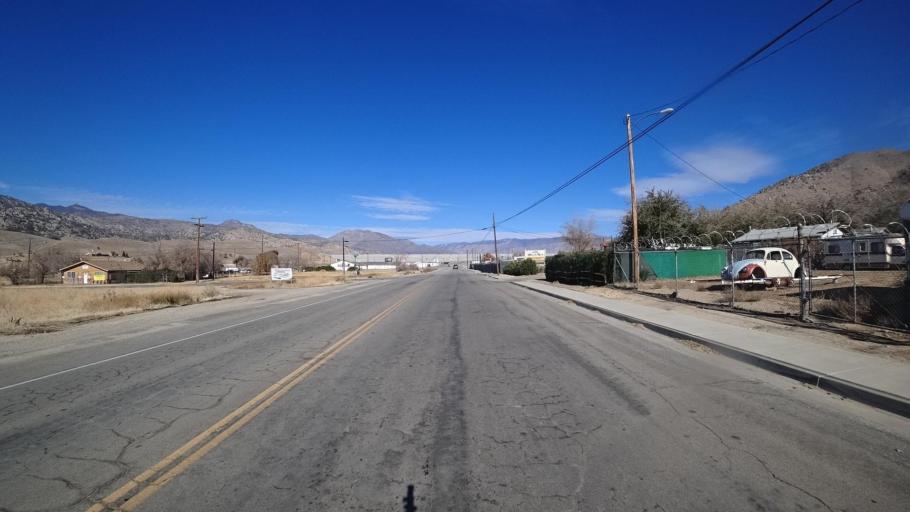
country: US
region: California
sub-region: Kern County
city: Lake Isabella
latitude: 35.6315
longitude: -118.4727
